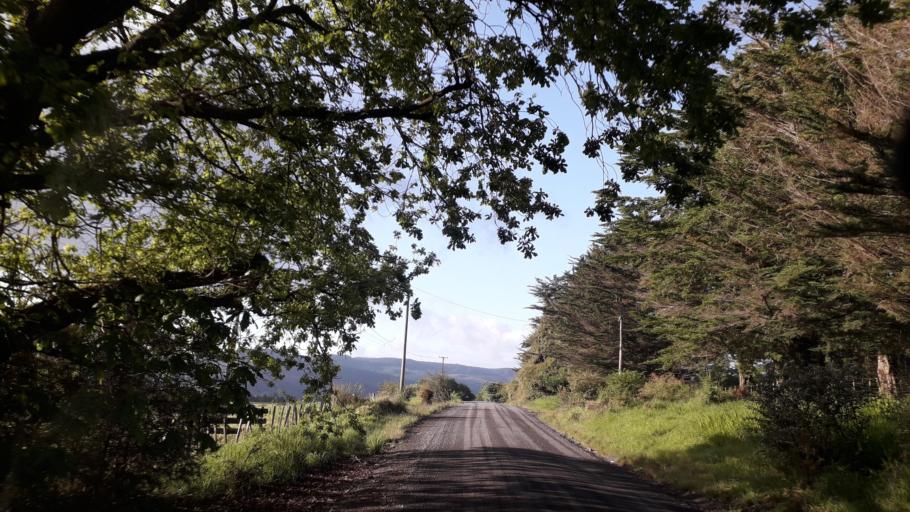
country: NZ
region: Northland
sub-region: Far North District
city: Waimate North
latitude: -35.4924
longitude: 173.6998
